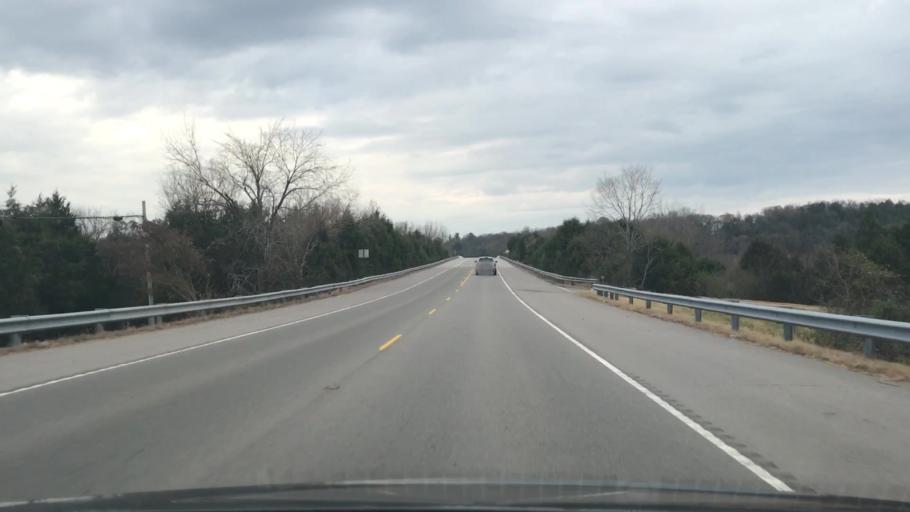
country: US
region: Tennessee
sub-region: Trousdale County
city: Hartsville
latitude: 36.3695
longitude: -86.1762
